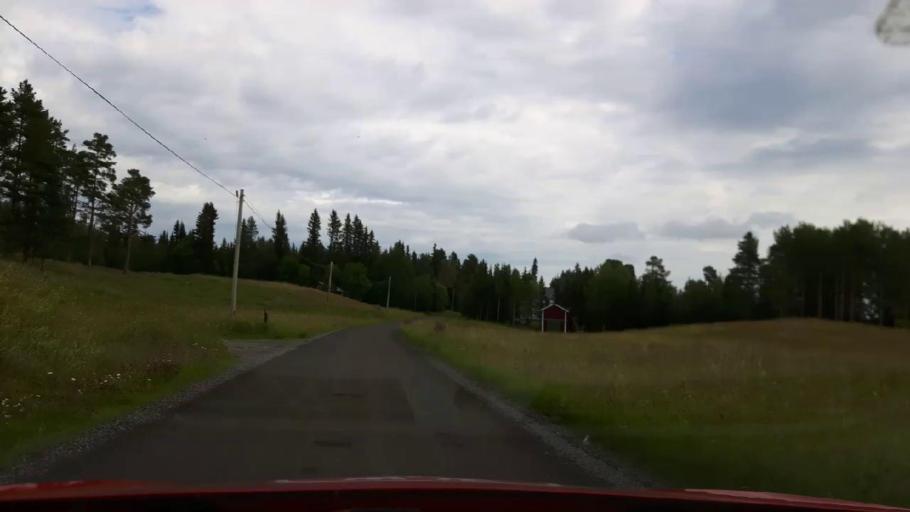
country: SE
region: Jaemtland
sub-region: OEstersunds Kommun
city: Lit
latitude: 63.4464
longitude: 15.2701
